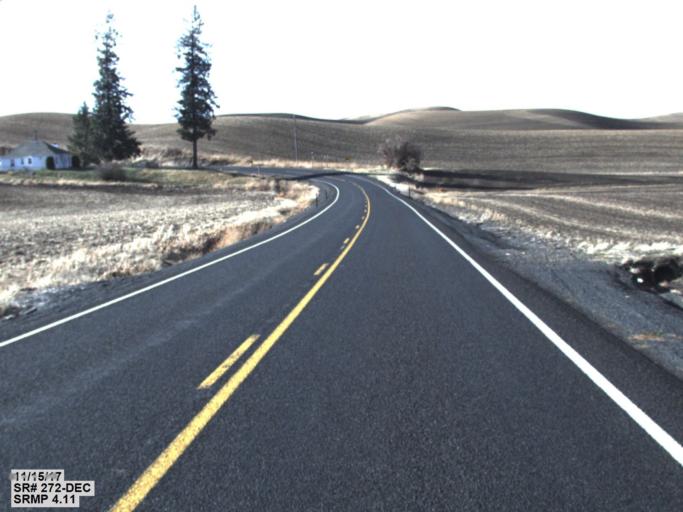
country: US
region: Washington
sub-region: Whitman County
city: Colfax
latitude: 46.9058
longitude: -117.2910
